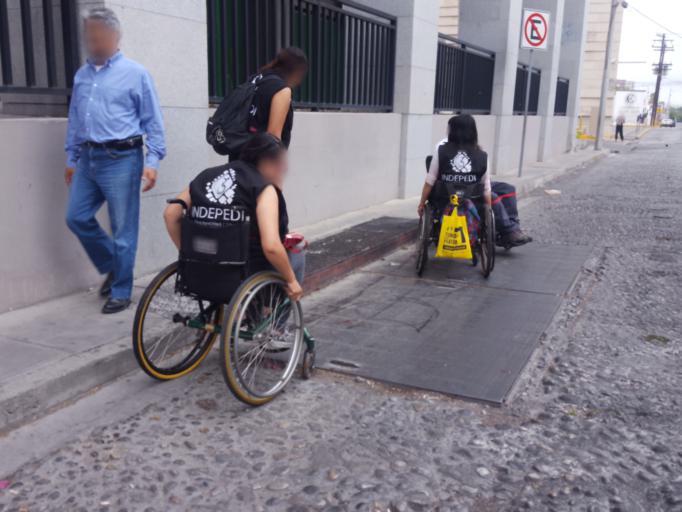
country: MX
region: Nuevo Leon
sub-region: Monterrey
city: Monterrey
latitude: 25.6706
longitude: -100.3074
